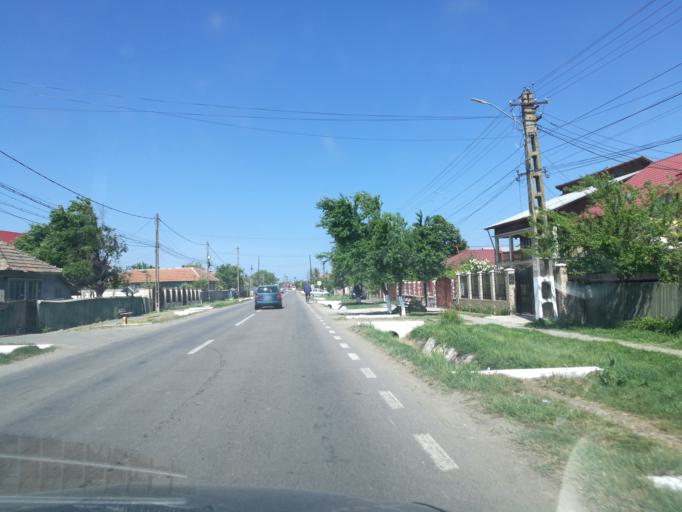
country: RO
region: Prahova
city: Cioranii de Jos
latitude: 44.8195
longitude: 26.4150
